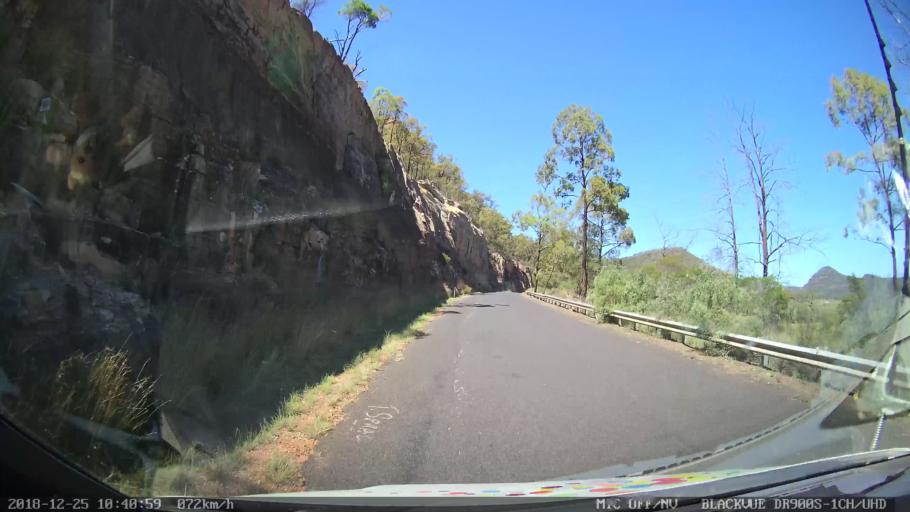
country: AU
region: New South Wales
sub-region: Upper Hunter Shire
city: Merriwa
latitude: -32.4131
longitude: 150.3394
